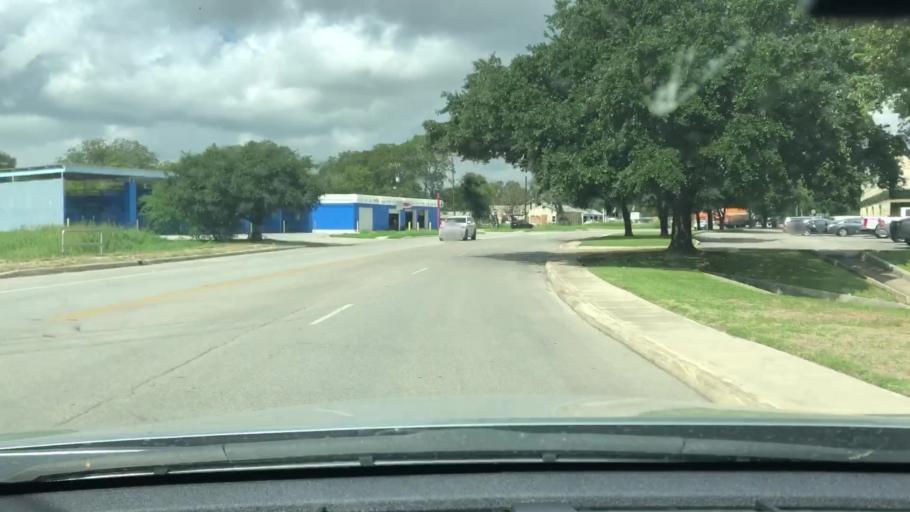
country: US
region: Texas
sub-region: Bexar County
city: Windcrest
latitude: 29.5317
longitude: -98.3778
